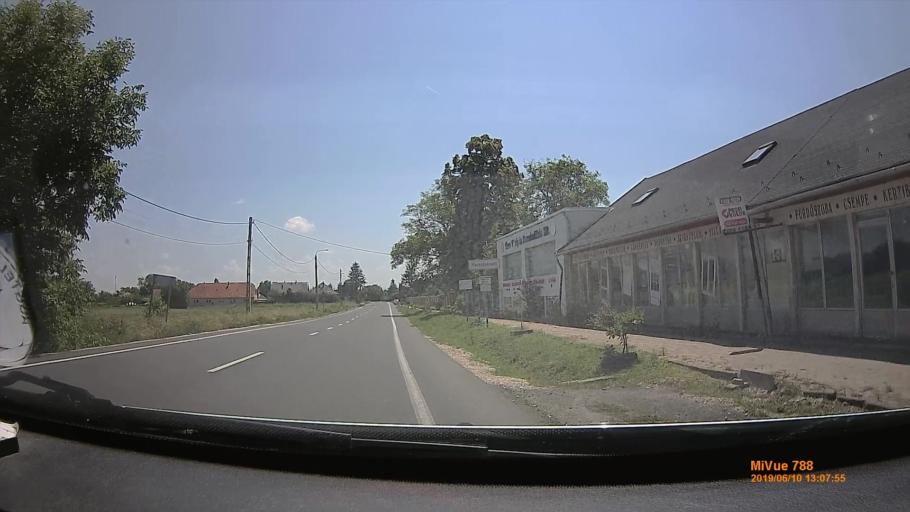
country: HU
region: Borsod-Abauj-Zemplen
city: Gesztely
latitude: 48.0837
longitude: 20.9702
